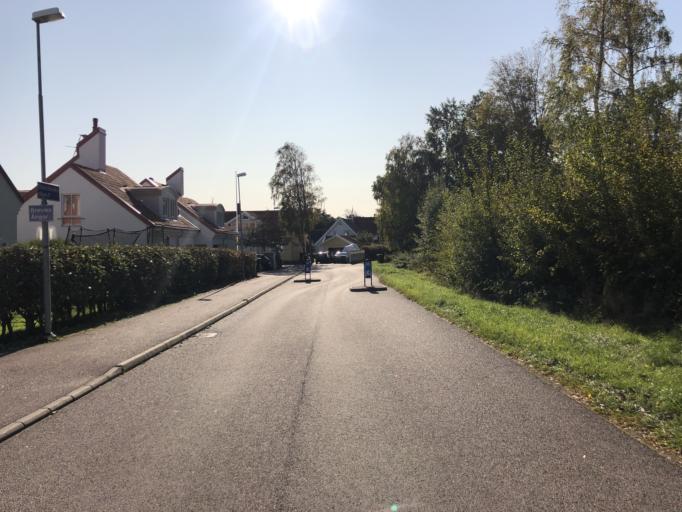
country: SE
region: Vaestra Goetaland
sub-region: Goteborg
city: Billdal
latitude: 57.6193
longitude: 11.8857
